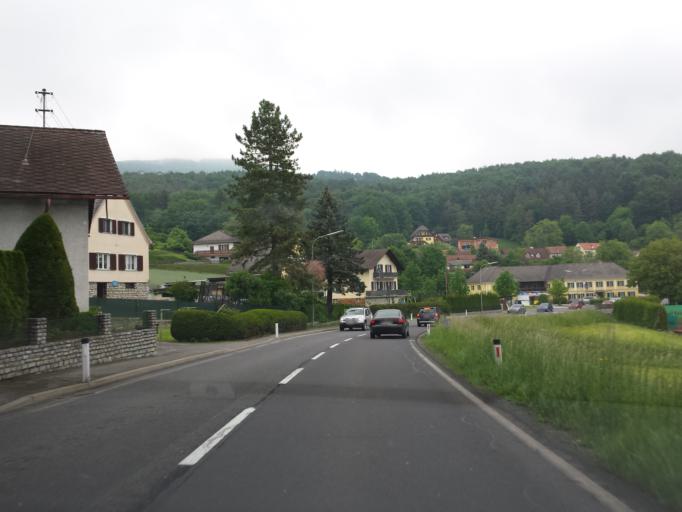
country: AT
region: Styria
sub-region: Politischer Bezirk Weiz
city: Puch bei Weiz
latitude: 47.2275
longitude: 15.6740
